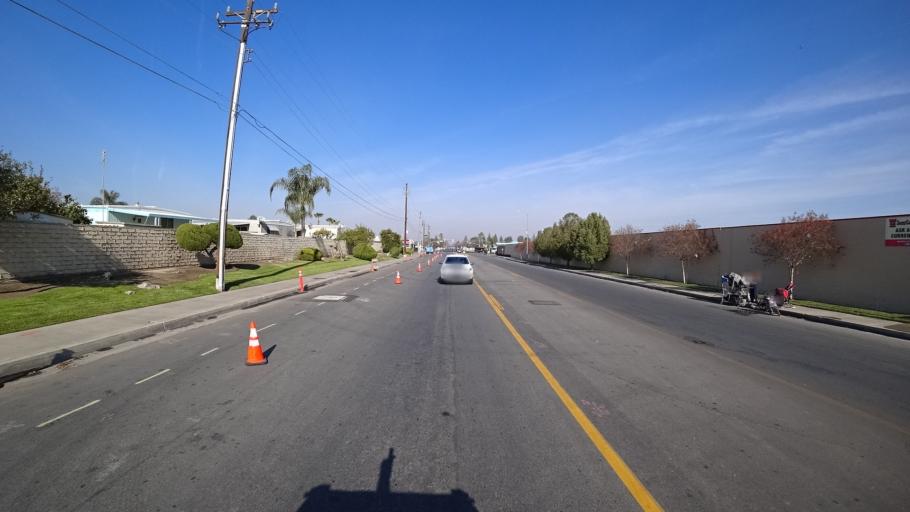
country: US
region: California
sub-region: Kern County
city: Greenfield
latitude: 35.3158
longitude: -119.0301
